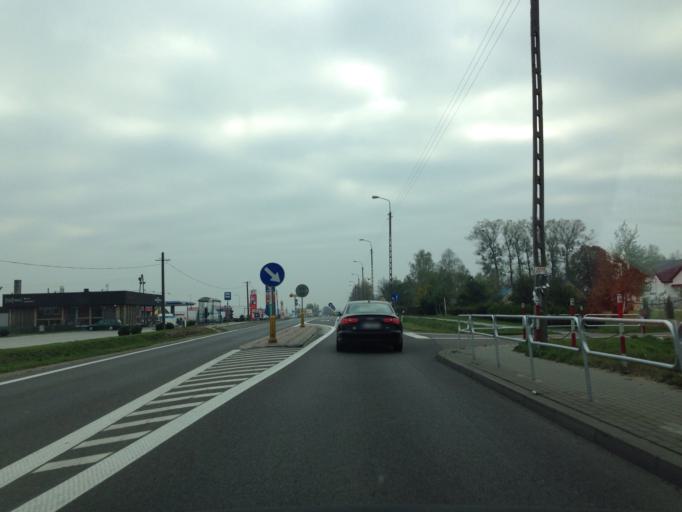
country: PL
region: Masovian Voivodeship
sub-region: Powiat plocki
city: Drobin
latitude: 52.7357
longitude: 19.9974
